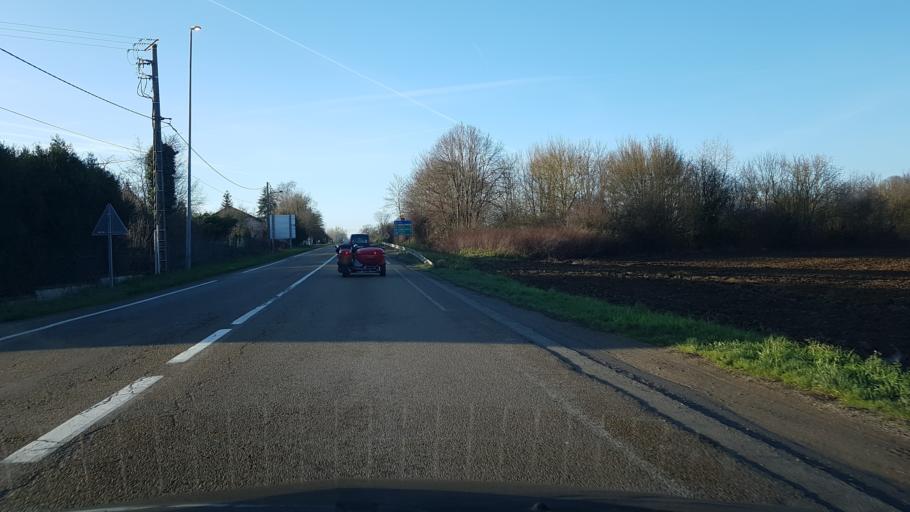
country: FR
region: Champagne-Ardenne
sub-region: Departement de la Marne
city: Vitry-le-Francois
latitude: 48.7355
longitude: 4.5528
